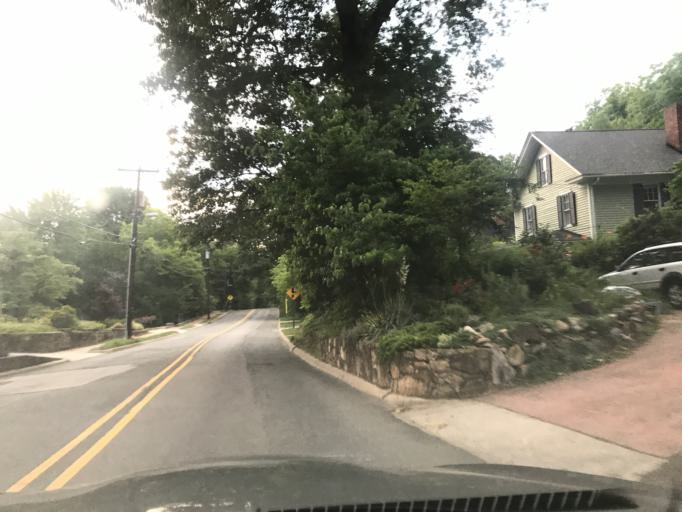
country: US
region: North Carolina
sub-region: Orange County
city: Chapel Hill
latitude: 35.9168
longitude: -79.0499
